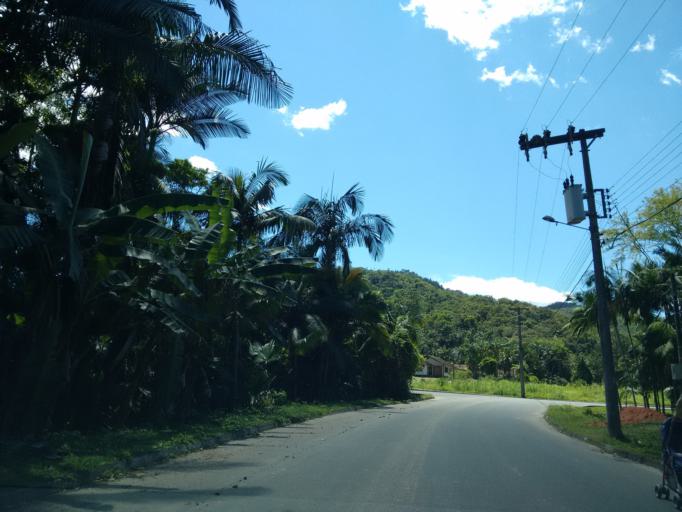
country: BR
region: Santa Catarina
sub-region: Pomerode
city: Pomerode
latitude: -26.7359
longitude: -49.1729
